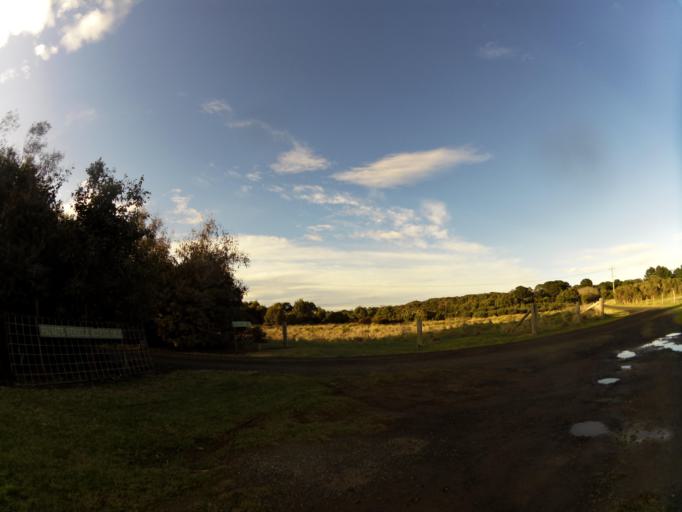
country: AU
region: Victoria
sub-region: Bass Coast
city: North Wonthaggi
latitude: -38.6055
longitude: 145.5745
